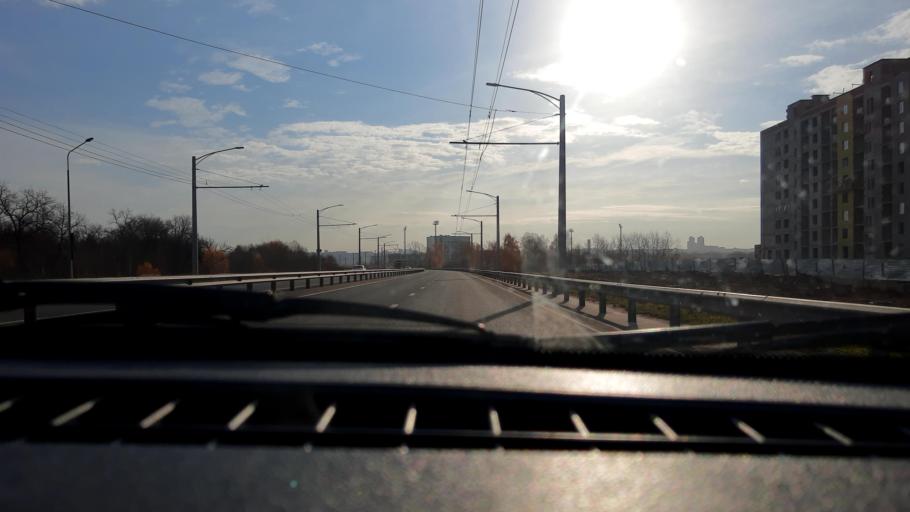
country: RU
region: Bashkortostan
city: Mikhaylovka
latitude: 54.7722
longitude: 55.9015
